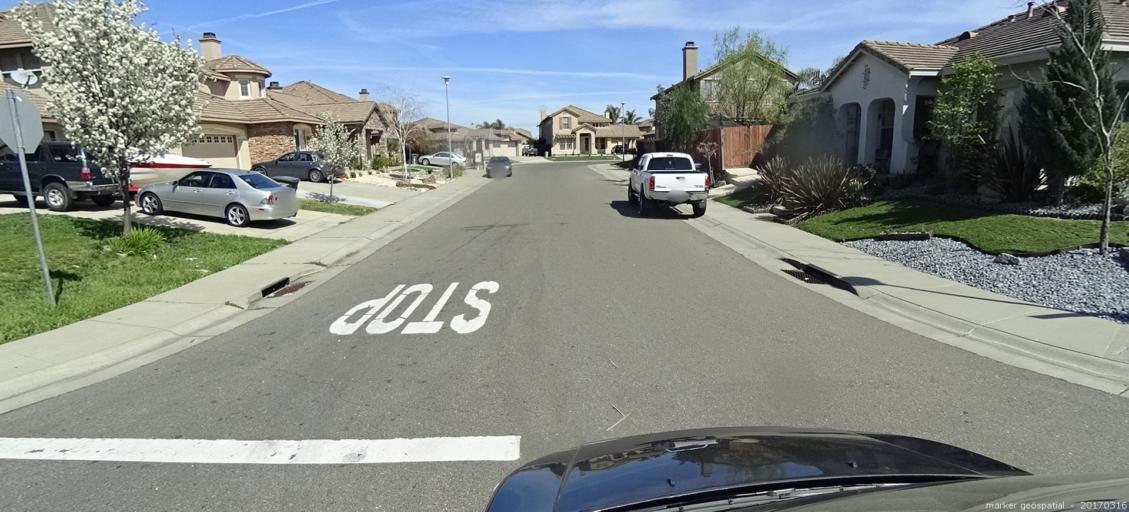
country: US
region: California
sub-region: Sacramento County
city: Parkway
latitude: 38.4744
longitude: -121.4919
